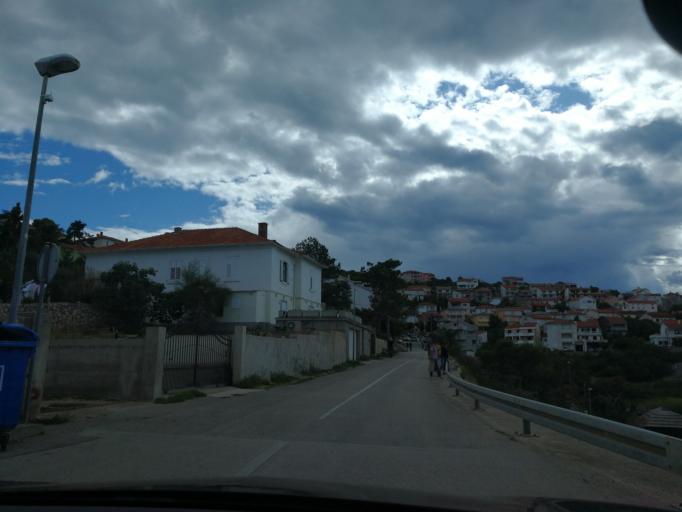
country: HR
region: Primorsko-Goranska
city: Punat
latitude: 45.0759
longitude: 14.6798
